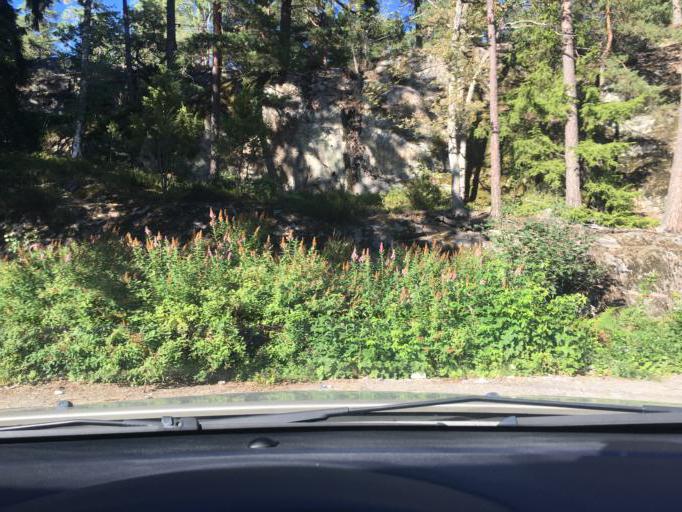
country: SE
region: Stockholm
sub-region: Nacka Kommun
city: Boo
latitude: 59.3266
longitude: 18.2412
